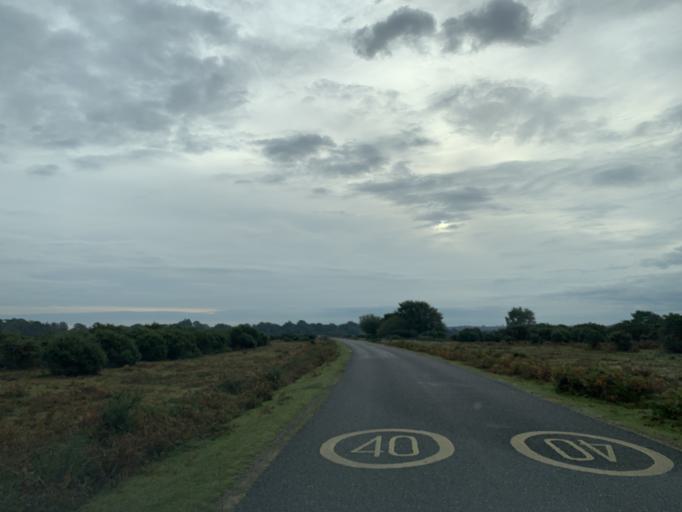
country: GB
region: England
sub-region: Hampshire
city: Sway
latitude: 50.8213
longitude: -1.6093
